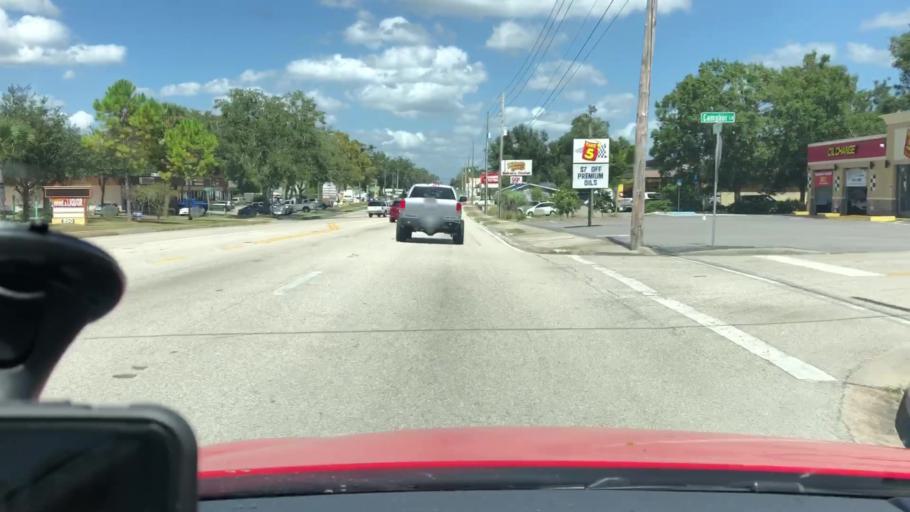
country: US
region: Florida
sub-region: Volusia County
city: West DeLand
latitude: 29.0227
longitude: -81.3240
